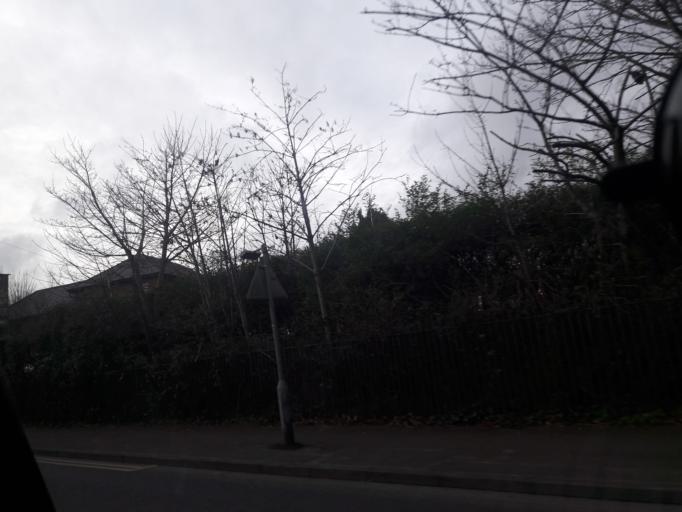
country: GB
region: Northern Ireland
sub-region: City of Belfast
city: Belfast
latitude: 54.6227
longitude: -5.9515
